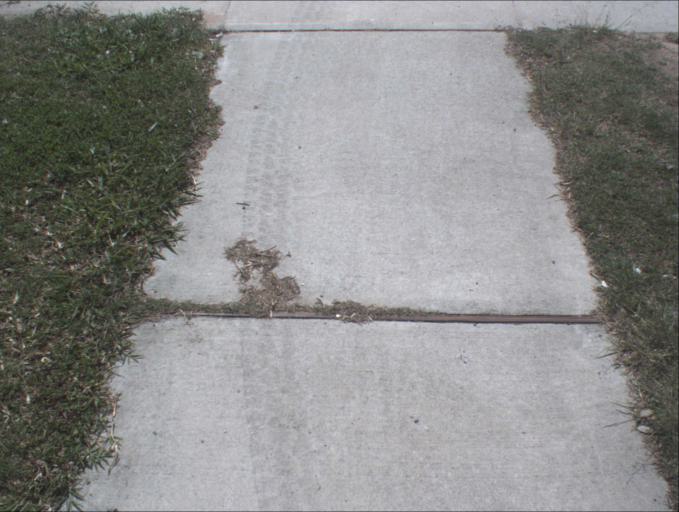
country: AU
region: Queensland
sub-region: Logan
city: Park Ridge South
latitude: -27.7312
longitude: 153.0373
